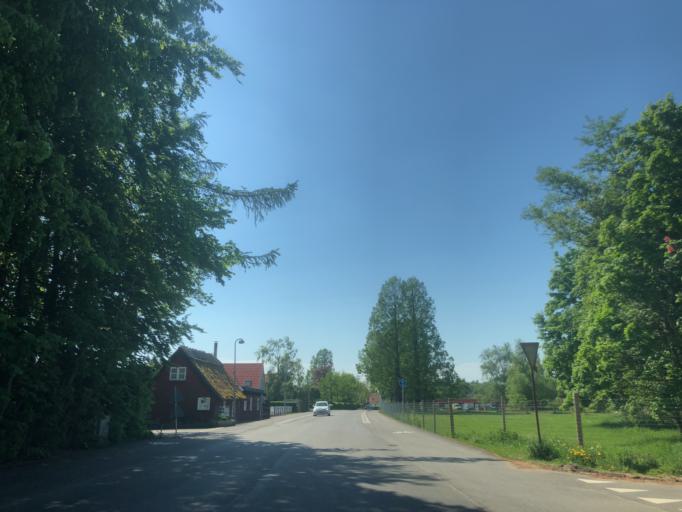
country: DK
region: Capital Region
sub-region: Hoje-Taastrup Kommune
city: Taastrup
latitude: 55.6264
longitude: 12.2545
